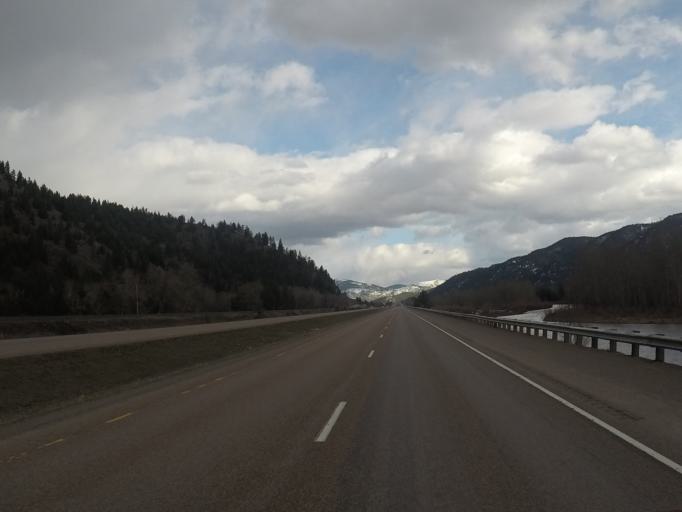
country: US
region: Montana
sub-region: Missoula County
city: Clinton
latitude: 46.8188
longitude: -113.7997
